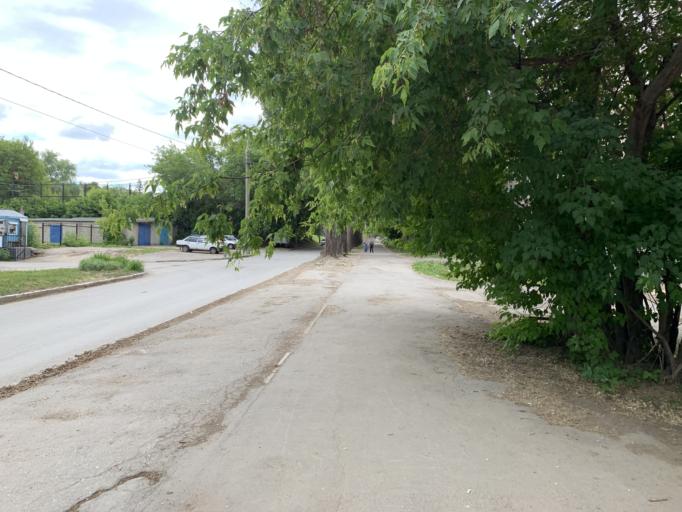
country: RU
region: Samara
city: Samara
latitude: 53.2143
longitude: 50.1721
